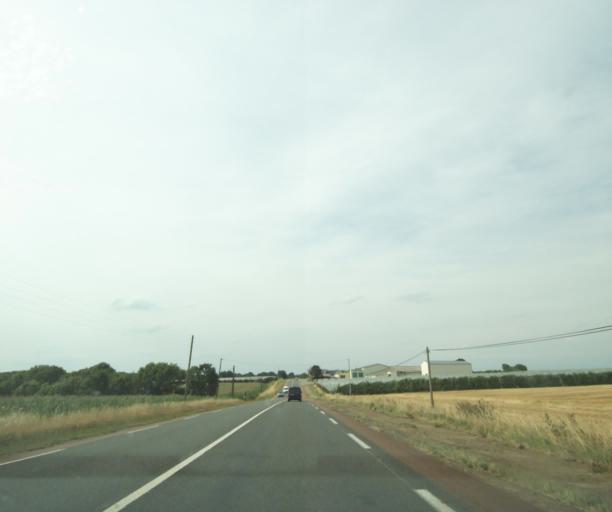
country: FR
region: Pays de la Loire
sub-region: Departement de la Sarthe
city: Luceau
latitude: 47.7339
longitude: 0.3932
